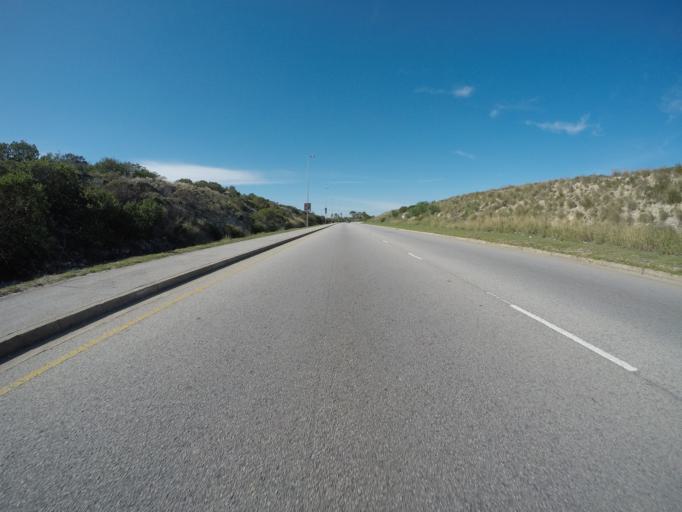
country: ZA
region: Eastern Cape
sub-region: Nelson Mandela Bay Metropolitan Municipality
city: Port Elizabeth
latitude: -33.9861
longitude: 25.6424
